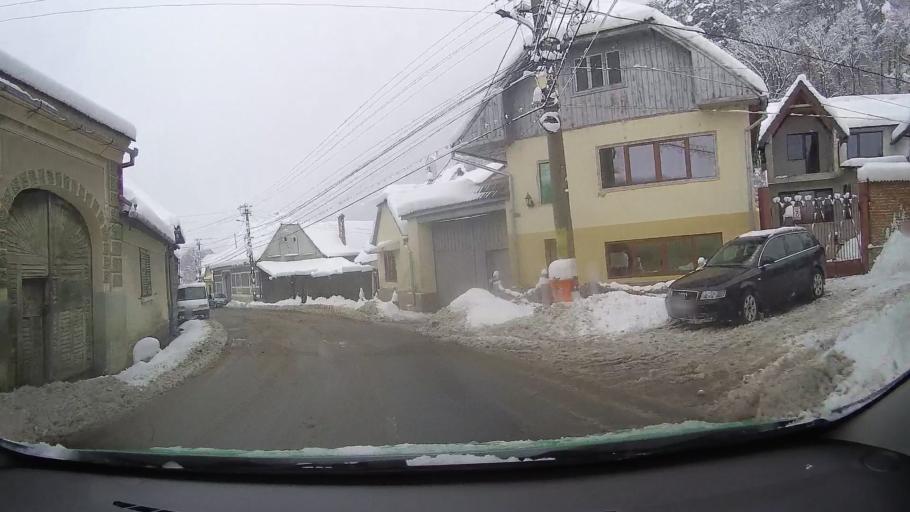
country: RO
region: Sibiu
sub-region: Comuna Tilisca
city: Tilisca
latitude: 45.7982
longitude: 23.8641
